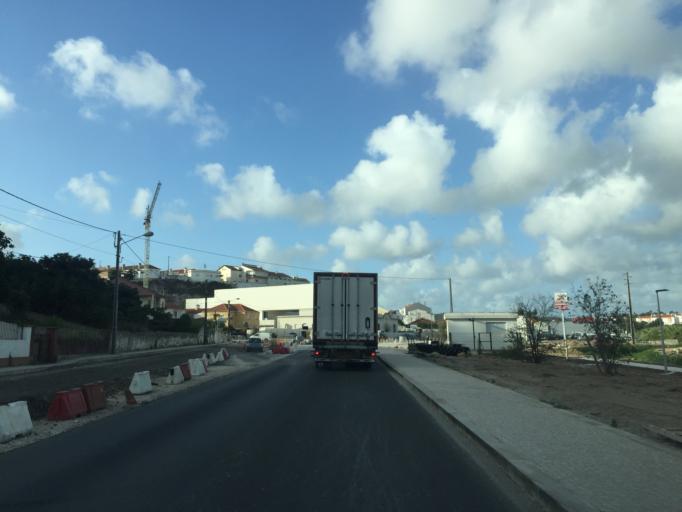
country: PT
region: Lisbon
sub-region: Torres Vedras
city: Torres Vedras
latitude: 39.0993
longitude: -9.2602
